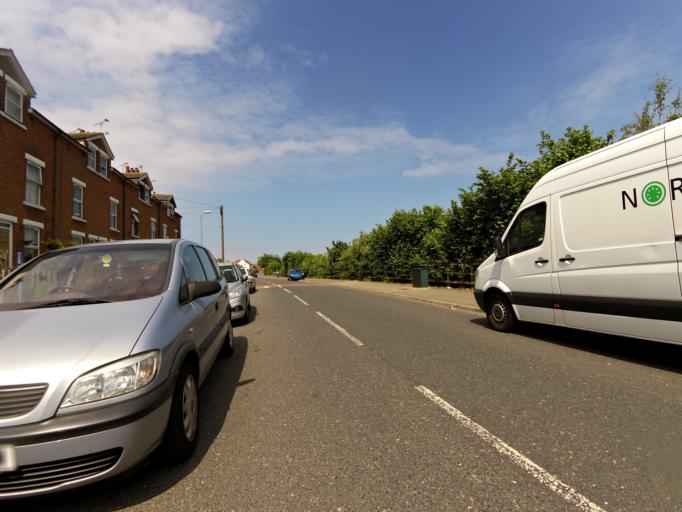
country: GB
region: England
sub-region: Suffolk
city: Bramford
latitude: 52.0708
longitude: 1.1254
